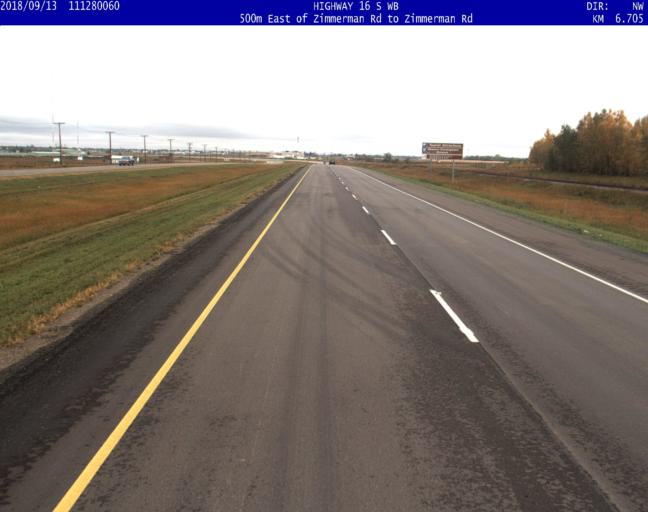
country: CA
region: Saskatchewan
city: Saskatoon
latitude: 52.0773
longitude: -106.5064
